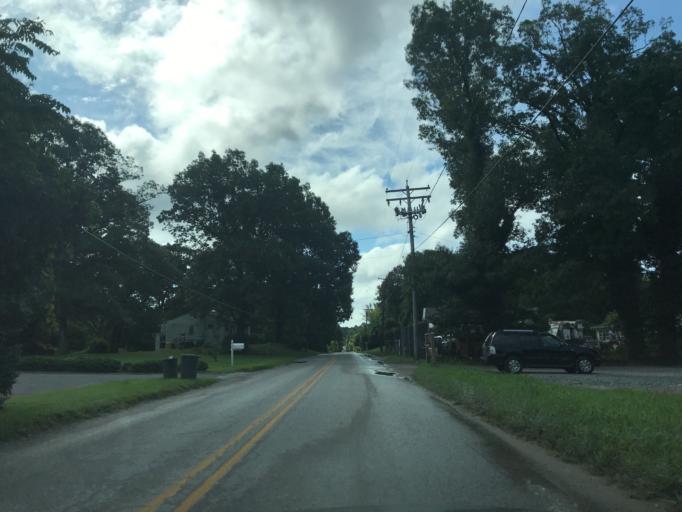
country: US
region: Maryland
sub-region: Anne Arundel County
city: Pasadena
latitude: 39.1177
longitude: -76.5634
